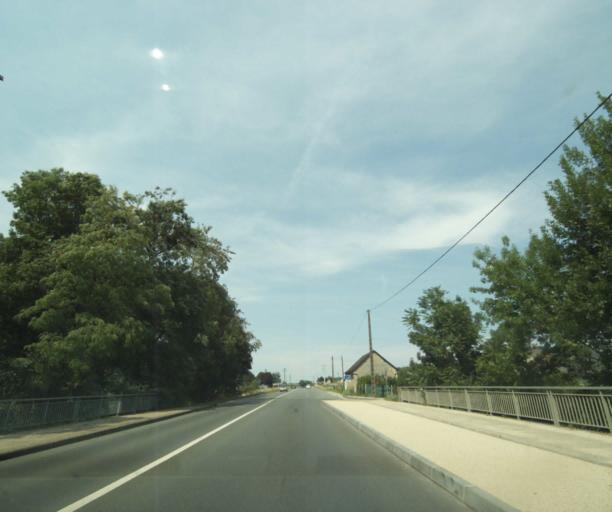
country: FR
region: Poitou-Charentes
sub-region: Departement de la Vienne
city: Antran
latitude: 46.8829
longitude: 0.5677
